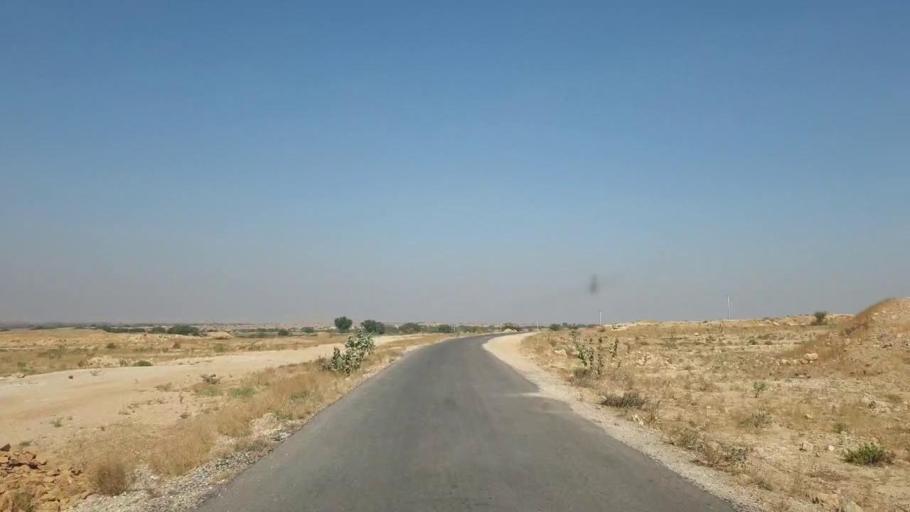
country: PK
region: Sindh
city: Thatta
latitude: 25.2050
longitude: 67.7974
